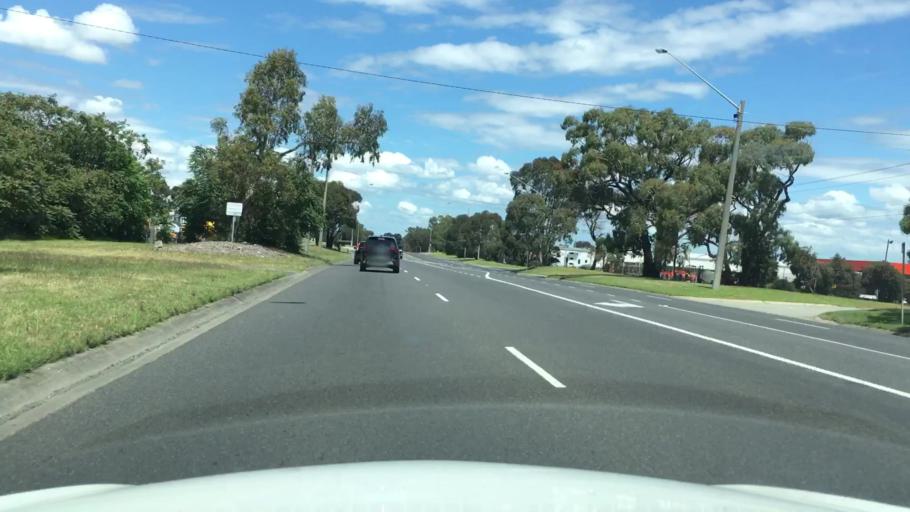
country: AU
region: Victoria
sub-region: Casey
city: Doveton
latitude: -38.0106
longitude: 145.2302
